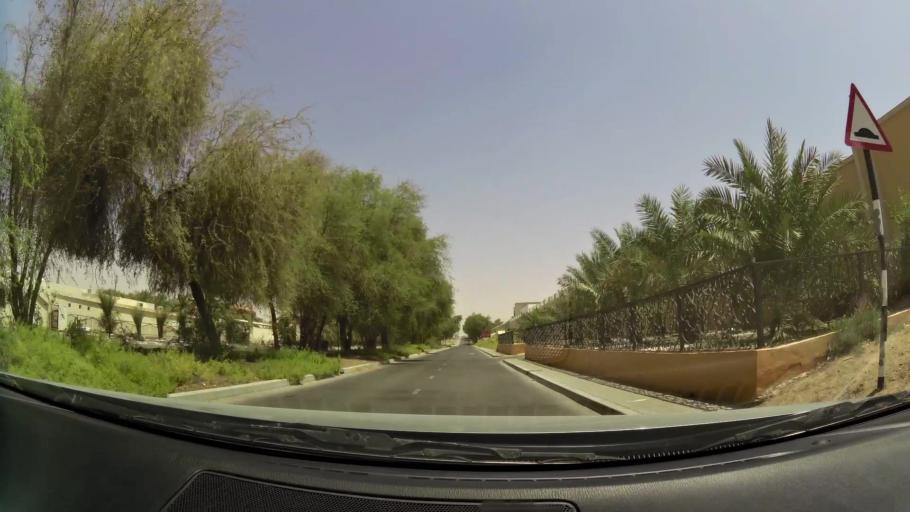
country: OM
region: Al Buraimi
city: Al Buraymi
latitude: 24.2739
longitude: 55.7484
